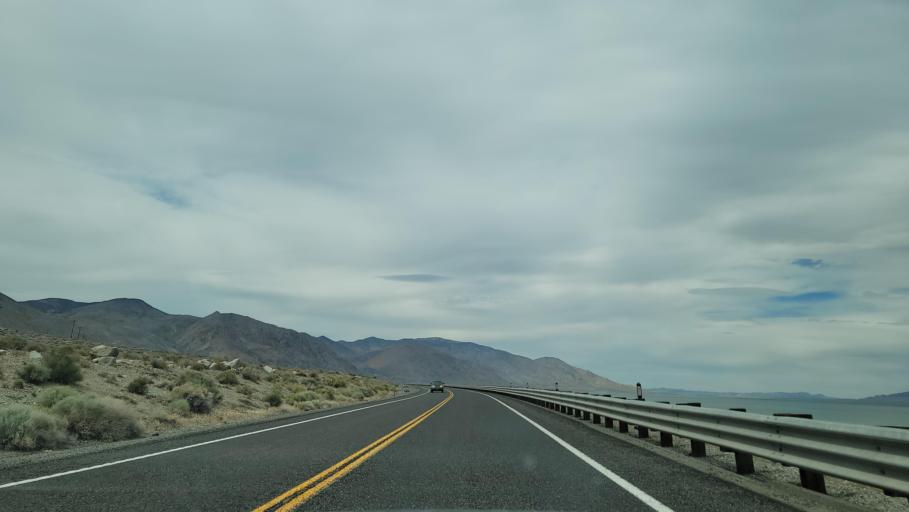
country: US
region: Nevada
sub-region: Mineral County
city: Hawthorne
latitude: 38.6052
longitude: -118.7116
